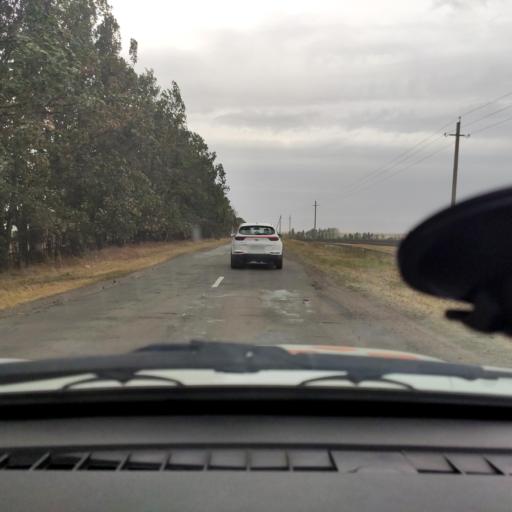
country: RU
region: Lipetsk
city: Khlevnoye
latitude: 52.0058
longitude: 39.1396
